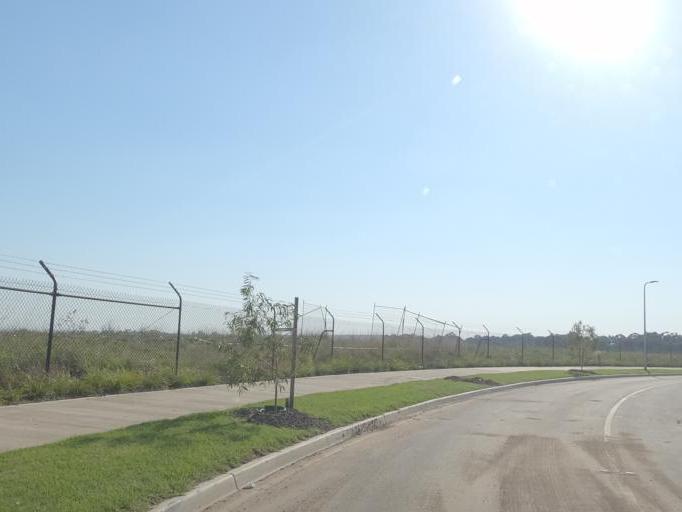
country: AU
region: Victoria
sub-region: Hume
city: Roxburgh Park
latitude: -37.6207
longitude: 144.9079
